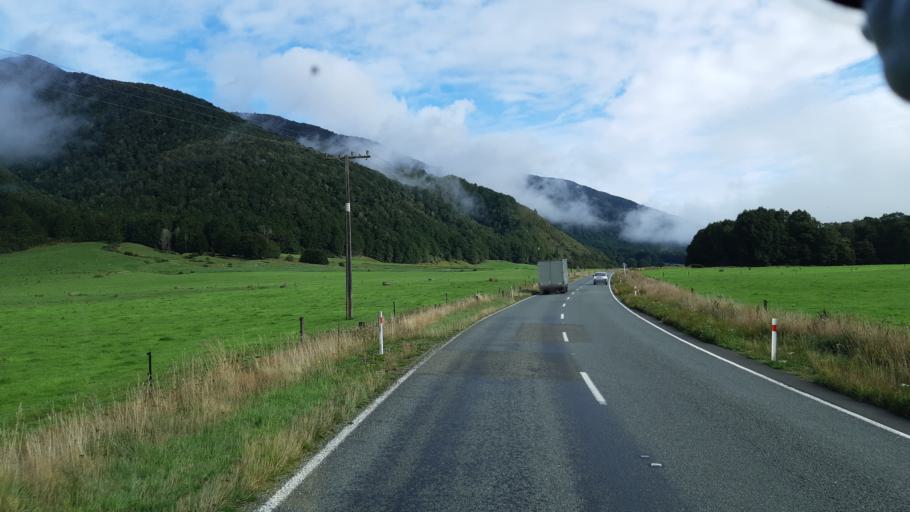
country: NZ
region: West Coast
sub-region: Buller District
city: Westport
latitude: -42.0492
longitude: 172.2564
